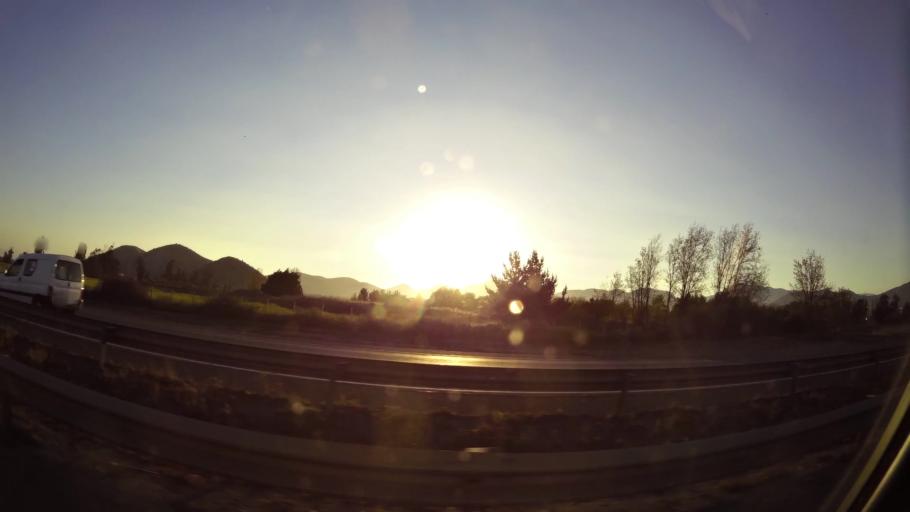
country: CL
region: Santiago Metropolitan
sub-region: Provincia de Santiago
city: Lo Prado
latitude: -33.5255
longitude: -70.7990
